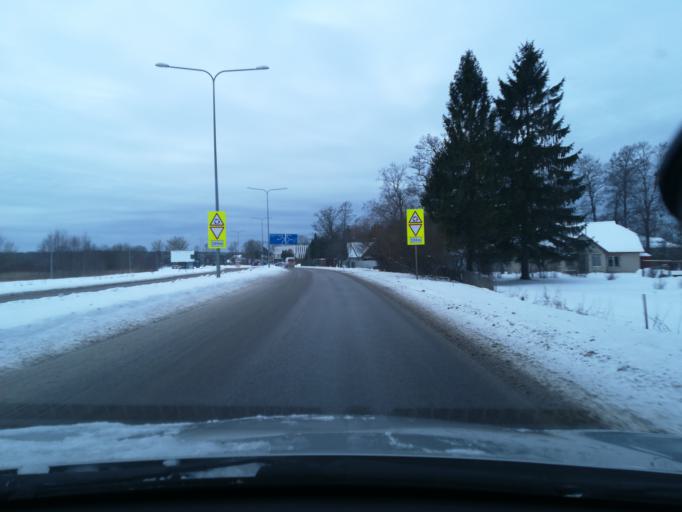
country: EE
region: Harju
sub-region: Harku vald
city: Tabasalu
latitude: 59.4369
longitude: 24.5775
